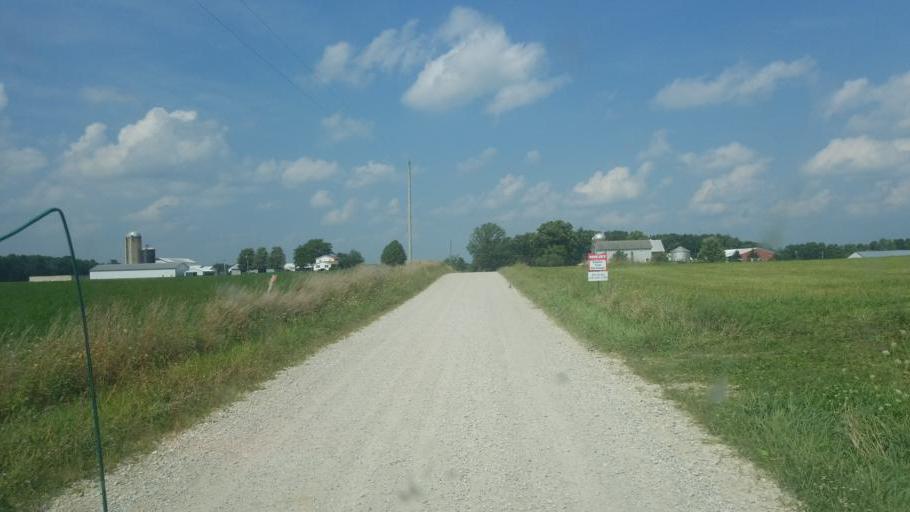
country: US
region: Ohio
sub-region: Huron County
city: New London
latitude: 40.9765
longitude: -82.4080
